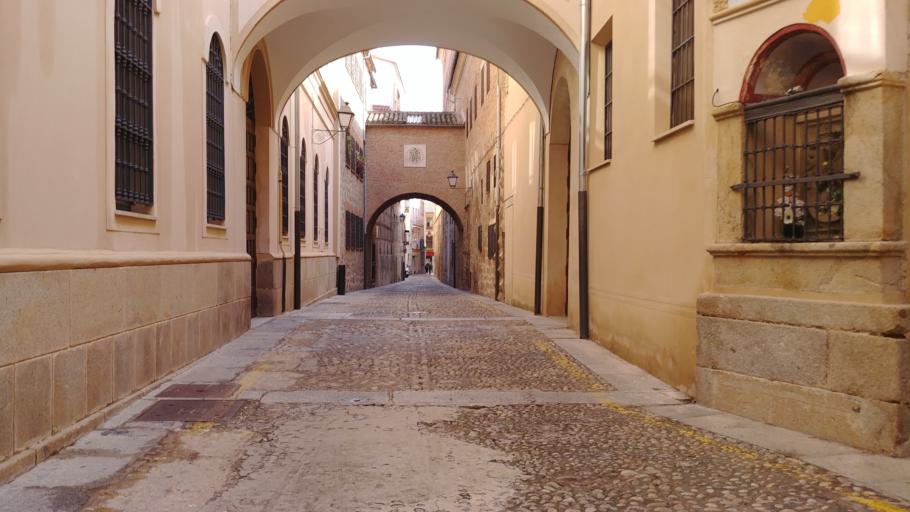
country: ES
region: Extremadura
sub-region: Provincia de Caceres
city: Plasencia
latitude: 40.0283
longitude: -6.0904
